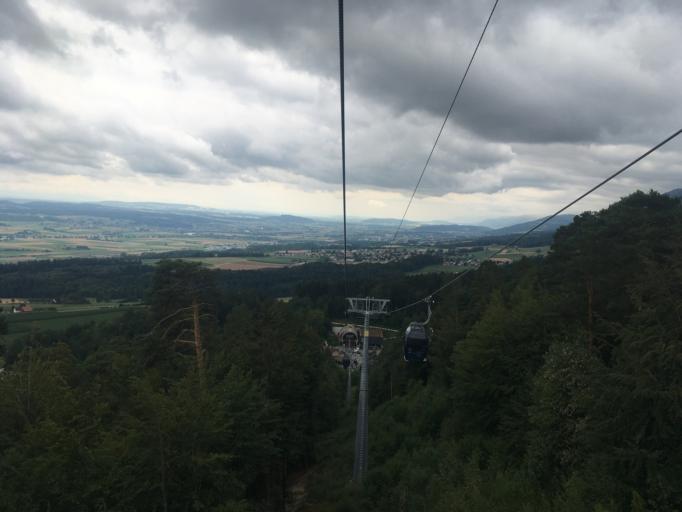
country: CH
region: Solothurn
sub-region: Bezirk Lebern
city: Langendorf
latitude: 47.2387
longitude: 7.4977
